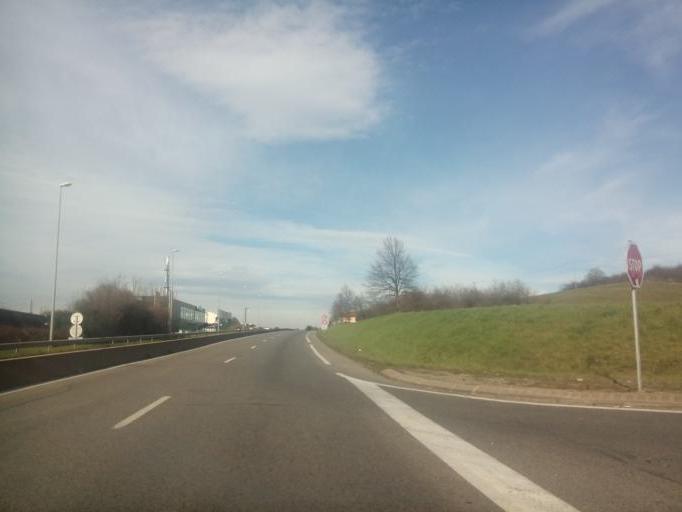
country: FR
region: Rhone-Alpes
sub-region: Departement du Rhone
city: Brignais
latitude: 45.6802
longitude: 4.7684
